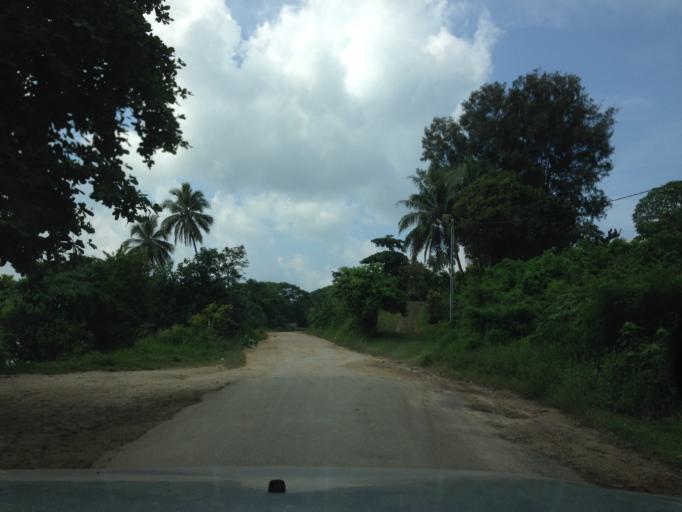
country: VU
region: Sanma
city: Luganville
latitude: -15.5474
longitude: 167.1469
